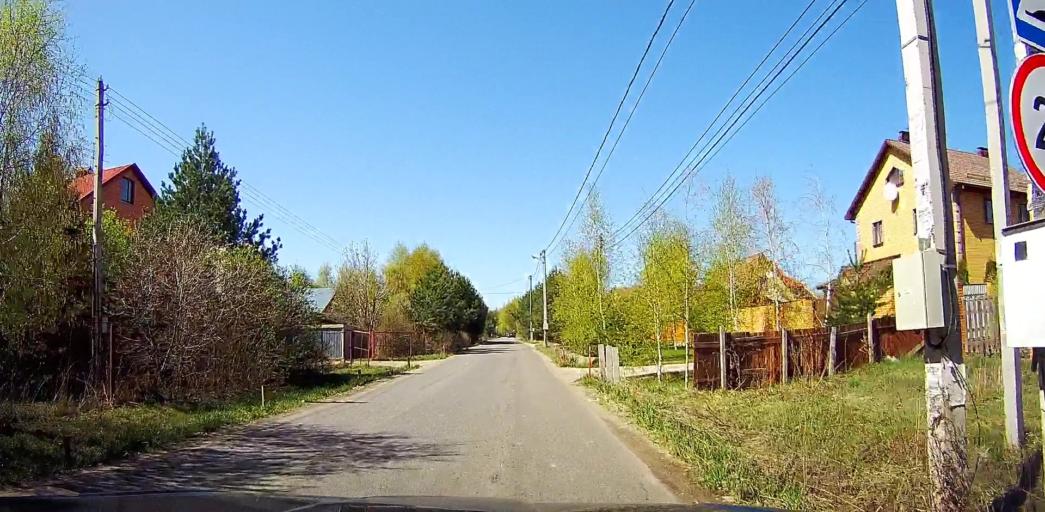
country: RU
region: Moskovskaya
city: Malyshevo
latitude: 55.4608
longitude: 38.3650
